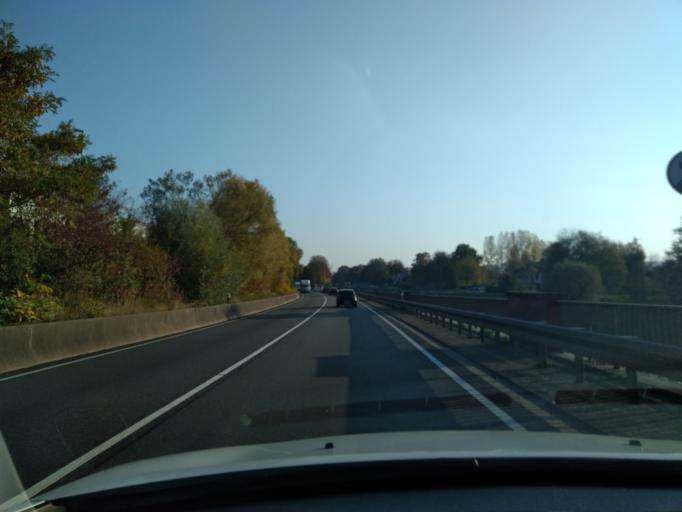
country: FR
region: Lorraine
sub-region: Departement de la Moselle
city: Grosbliederstroff
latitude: 49.1687
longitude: 7.0287
